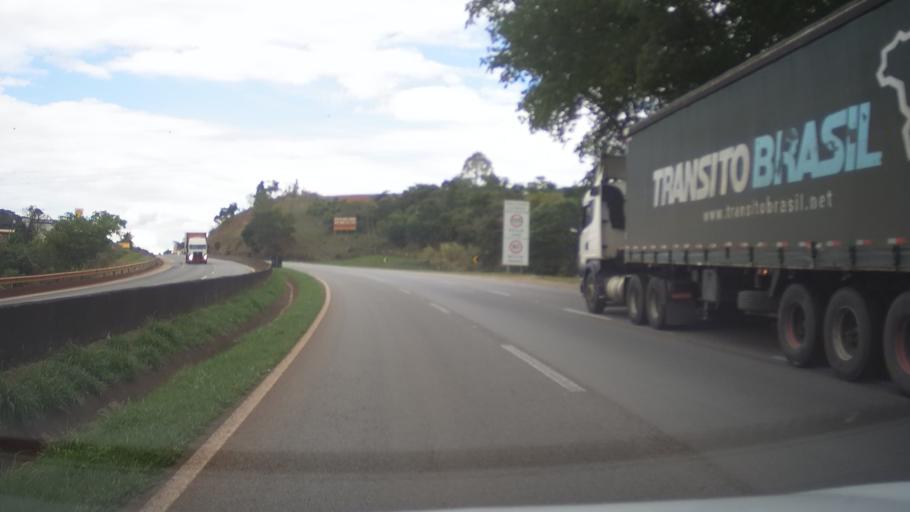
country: BR
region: Minas Gerais
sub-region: Igarape
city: Igarape
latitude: -20.2818
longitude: -44.4288
